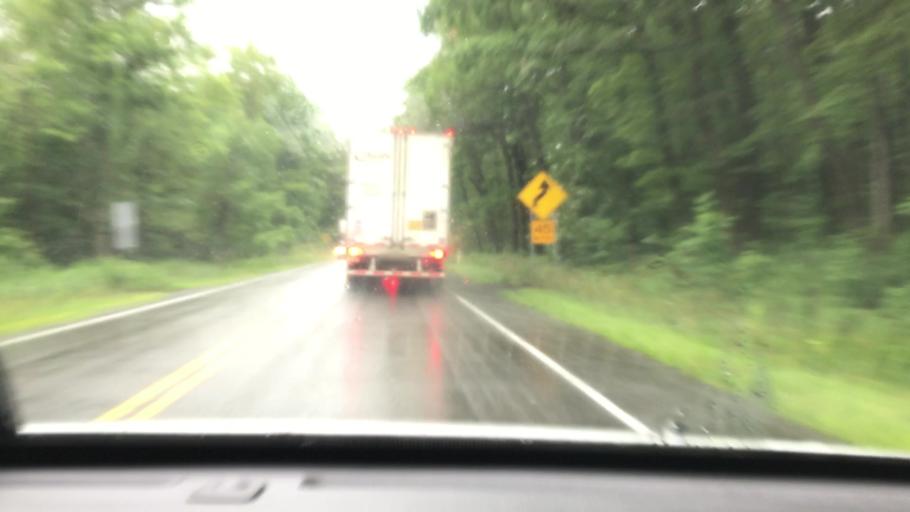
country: US
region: Pennsylvania
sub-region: Clearfield County
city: Osceola Mills
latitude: 40.7811
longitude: -78.2395
